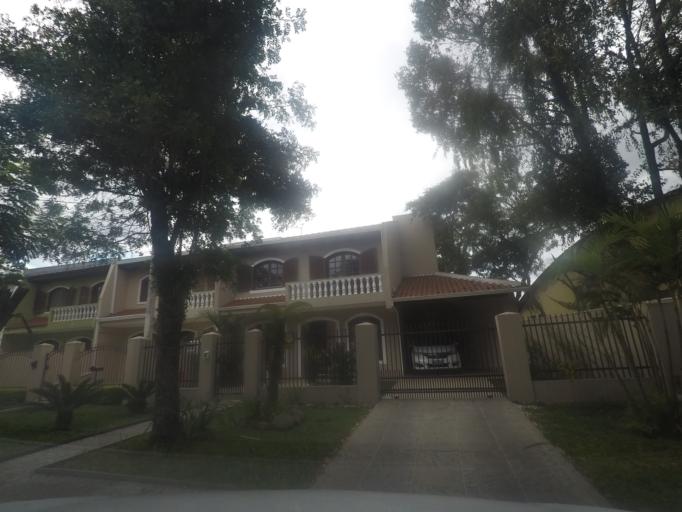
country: BR
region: Parana
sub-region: Pinhais
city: Pinhais
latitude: -25.4677
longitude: -49.2154
